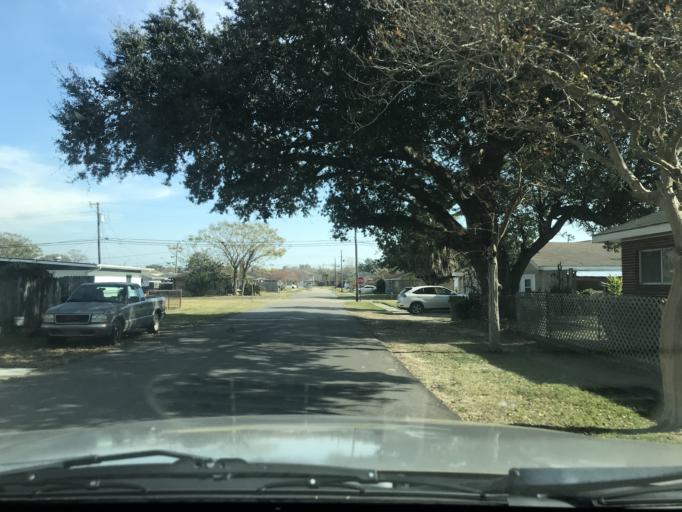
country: US
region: Louisiana
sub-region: Jefferson Parish
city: Marrero
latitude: 29.8909
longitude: -90.0895
